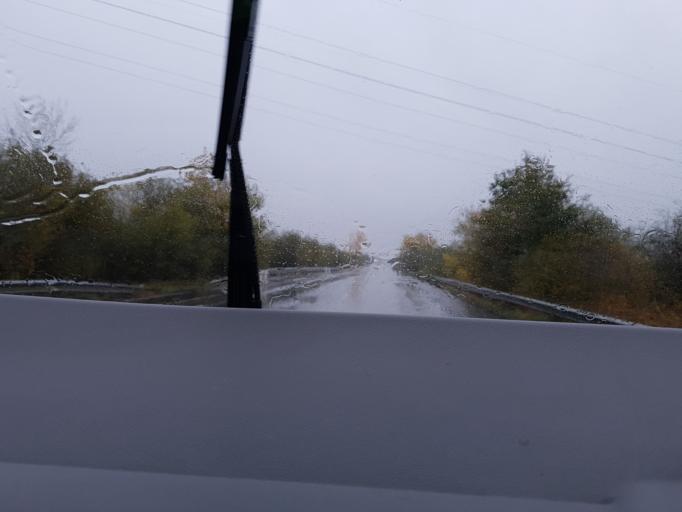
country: FR
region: Aquitaine
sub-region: Departement de la Gironde
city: Saint-Vincent-de-Paul
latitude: 44.9601
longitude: -0.4982
